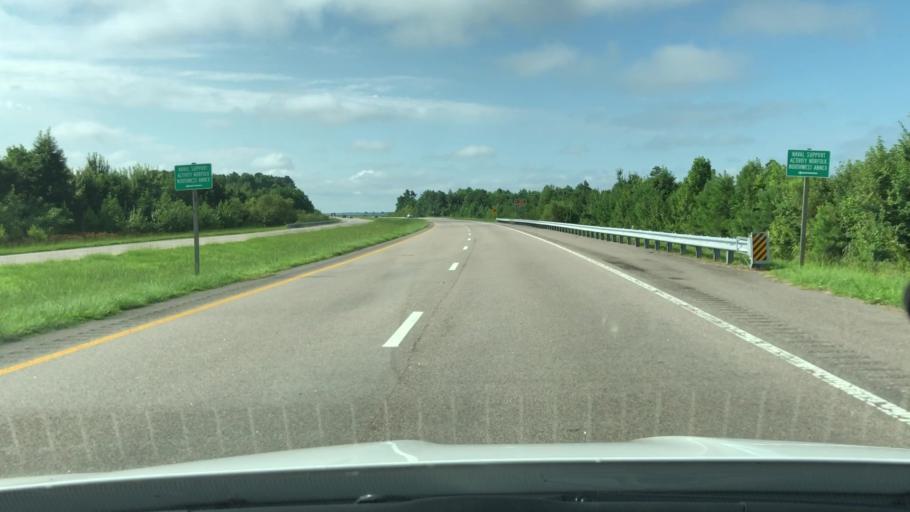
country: US
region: North Carolina
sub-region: Currituck County
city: Moyock
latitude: 36.6030
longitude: -76.3803
